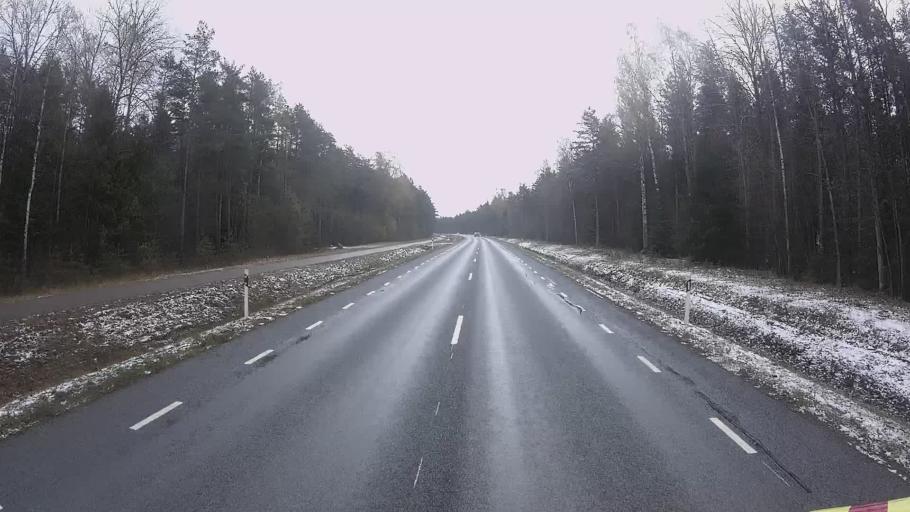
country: EE
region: Hiiumaa
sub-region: Kaerdla linn
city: Kardla
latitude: 58.9991
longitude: 22.7040
